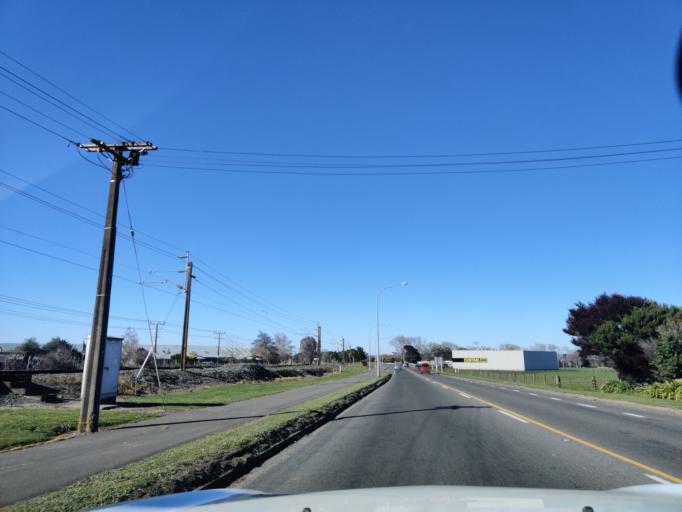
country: NZ
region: Manawatu-Wanganui
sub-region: Palmerston North City
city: Palmerston North
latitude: -40.2344
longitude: 175.5745
